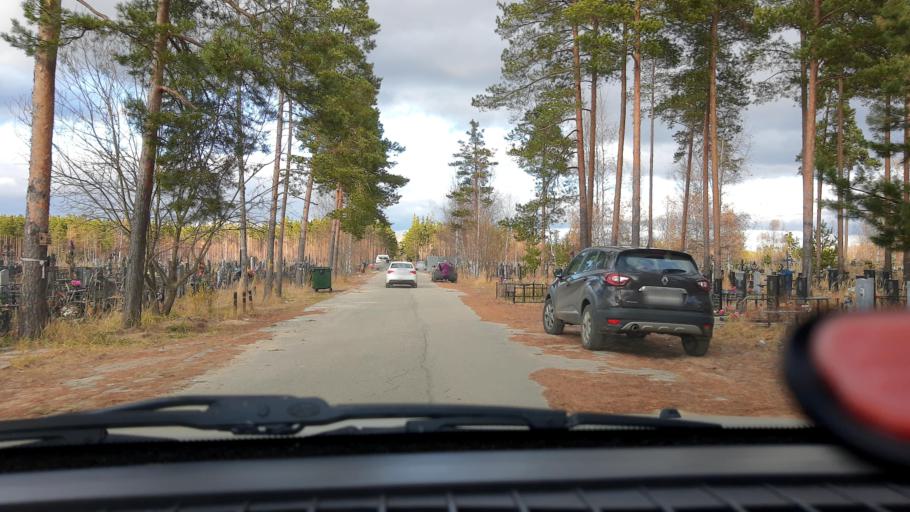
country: RU
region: Nizjnij Novgorod
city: Gorbatovka
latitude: 56.3610
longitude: 43.7707
